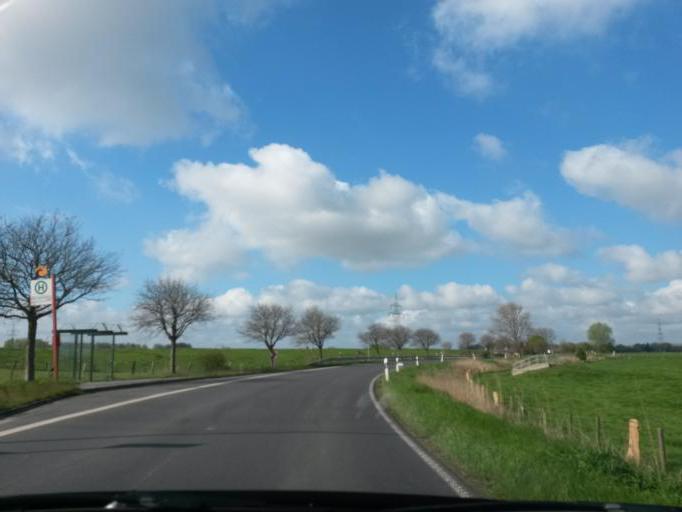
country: DE
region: Schleswig-Holstein
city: Holm
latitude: 53.6163
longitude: 9.6616
